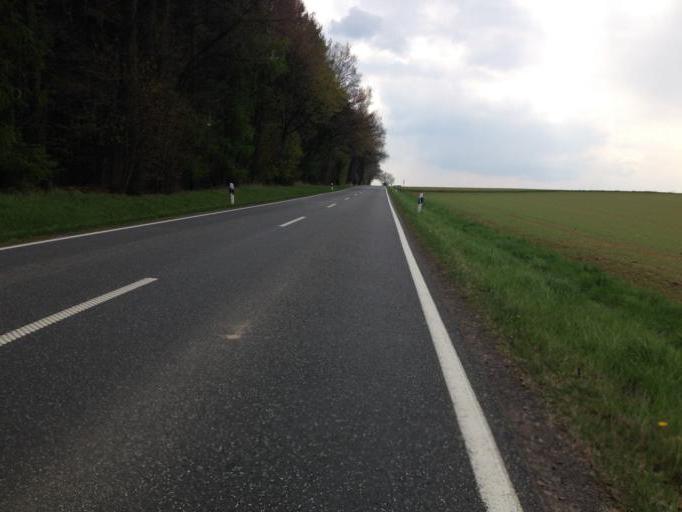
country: DE
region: Hesse
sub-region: Regierungsbezirk Giessen
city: Grunberg
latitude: 50.6256
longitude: 8.9829
